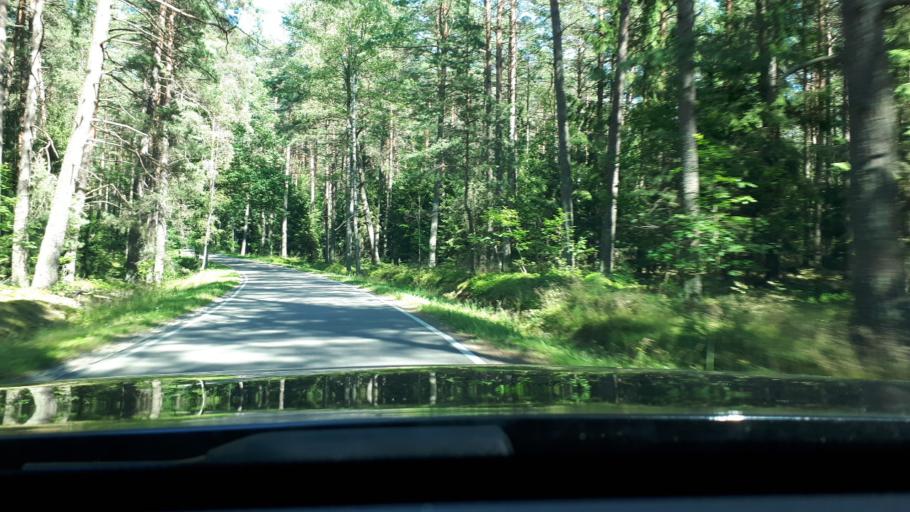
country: PL
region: Warmian-Masurian Voivodeship
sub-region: Powiat olsztynski
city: Stawiguda
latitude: 53.5882
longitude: 20.4426
